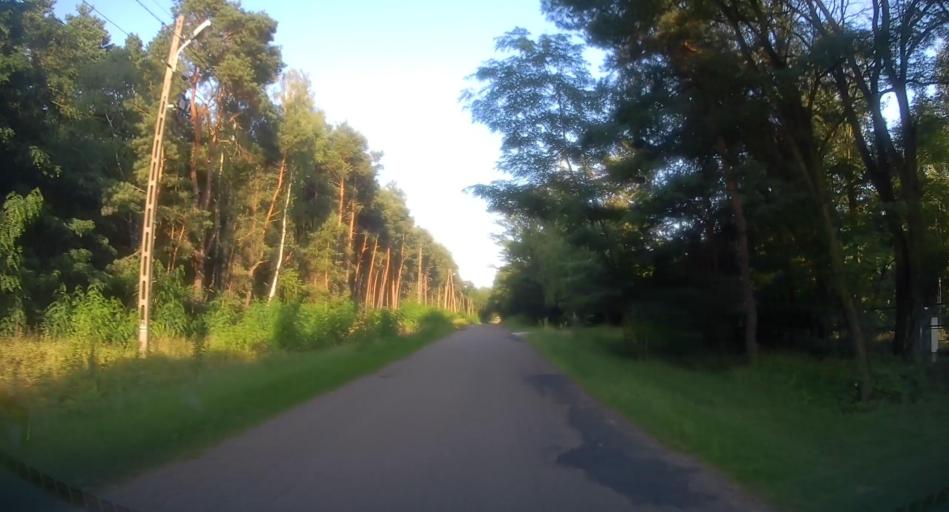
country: PL
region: Lodz Voivodeship
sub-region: Powiat skierniewicki
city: Kowiesy
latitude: 51.9048
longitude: 20.3556
